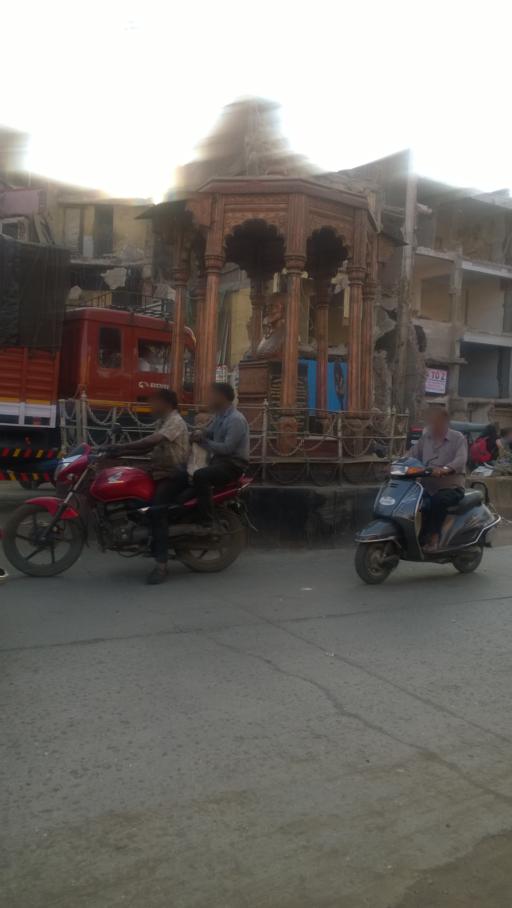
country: IN
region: Maharashtra
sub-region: Thane
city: Ulhasnagar
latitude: 19.2299
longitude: 73.1600
